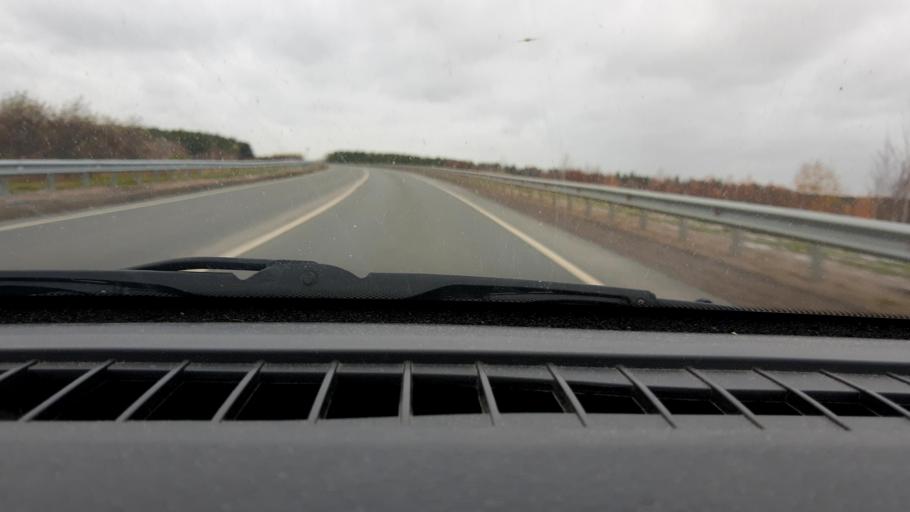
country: RU
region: Nizjnij Novgorod
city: Kstovo
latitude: 56.1502
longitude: 44.1592
